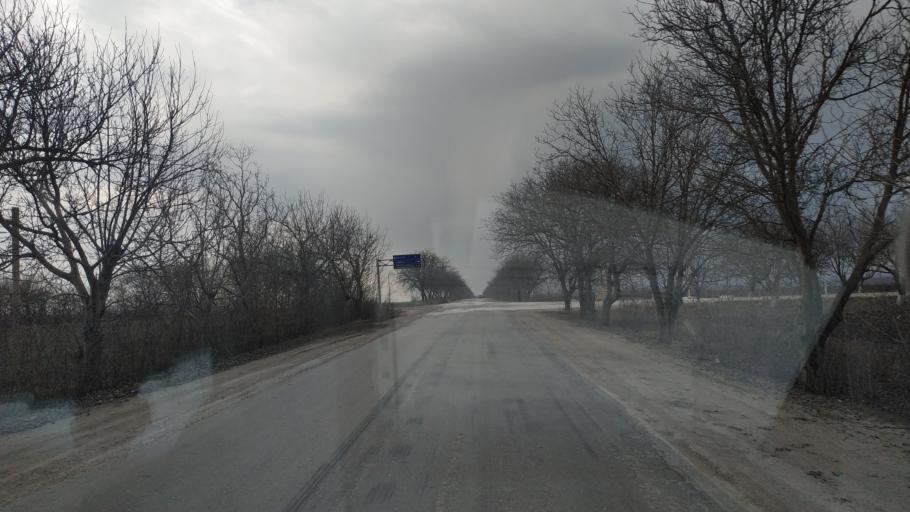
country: MD
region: Telenesti
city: Grigoriopol
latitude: 47.0296
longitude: 29.2919
